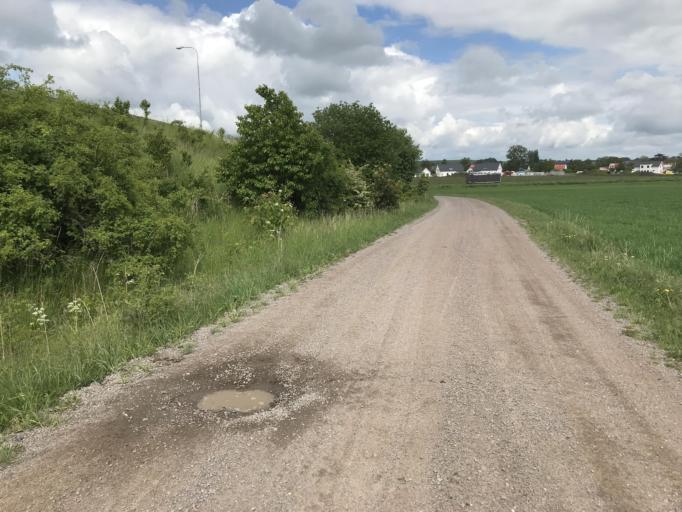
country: SE
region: Skane
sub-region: Landskrona
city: Landskrona
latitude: 55.8932
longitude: 12.8559
